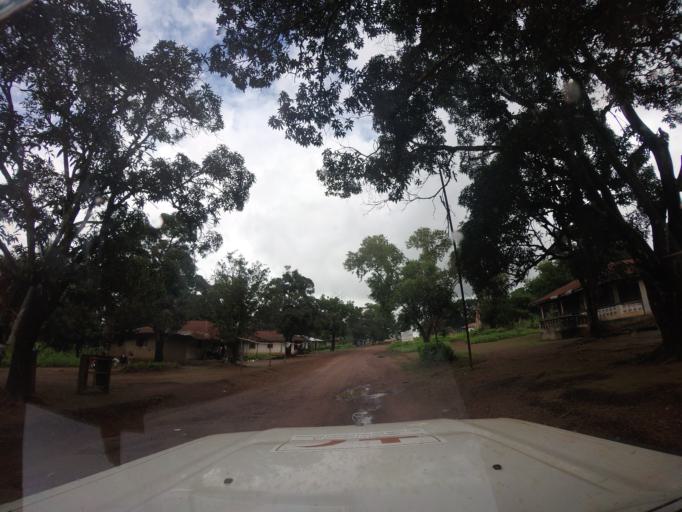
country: SL
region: Northern Province
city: Kukuna
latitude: 9.2849
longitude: -12.6718
